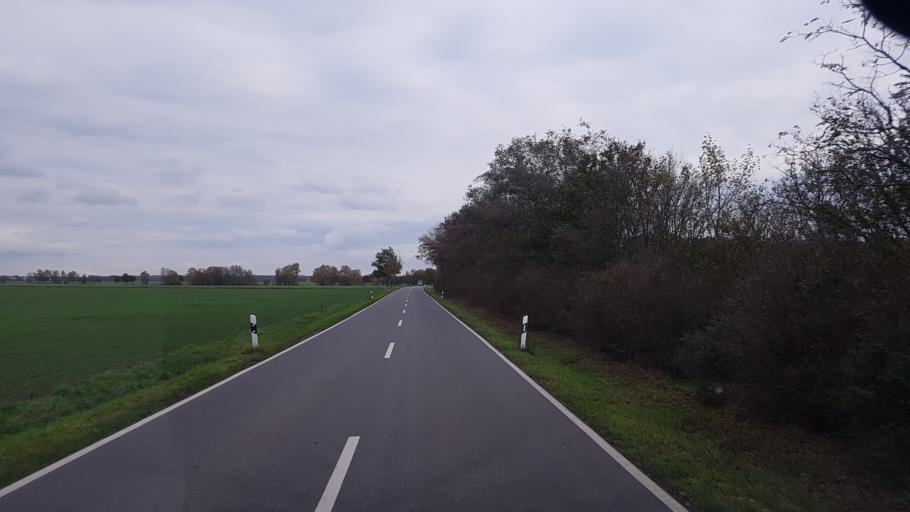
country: DE
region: Brandenburg
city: Finsterwalde
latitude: 51.6104
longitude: 13.6594
